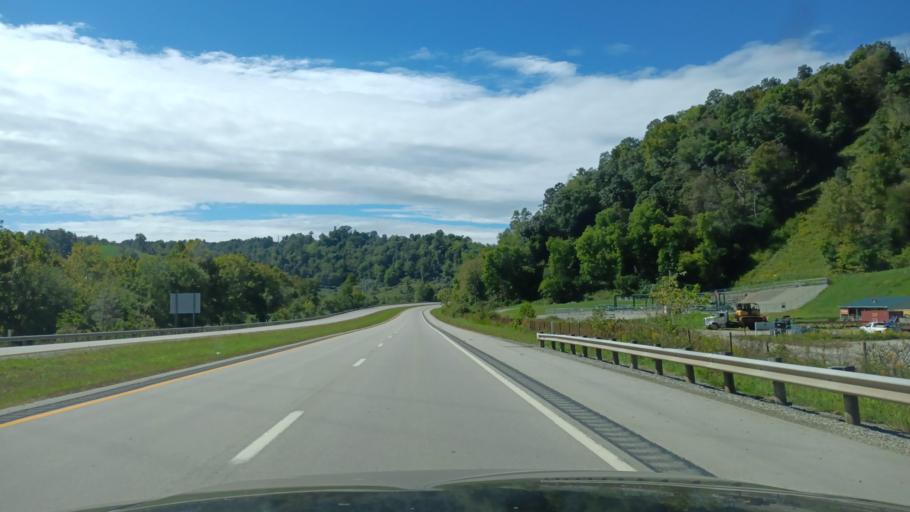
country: US
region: West Virginia
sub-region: Doddridge County
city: West Union
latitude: 39.2795
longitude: -80.6821
